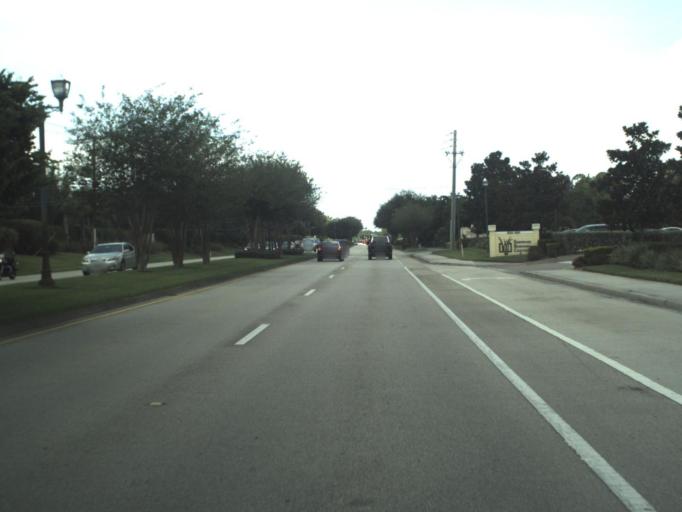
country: US
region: Florida
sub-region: Martin County
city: Palm City
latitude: 27.1625
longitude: -80.2362
